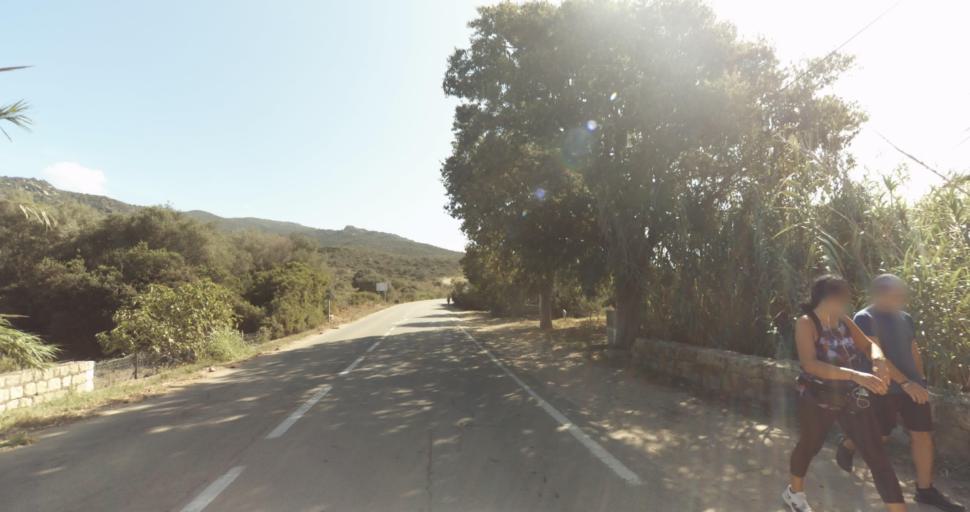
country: FR
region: Corsica
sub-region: Departement de la Corse-du-Sud
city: Ajaccio
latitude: 41.9109
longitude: 8.6455
